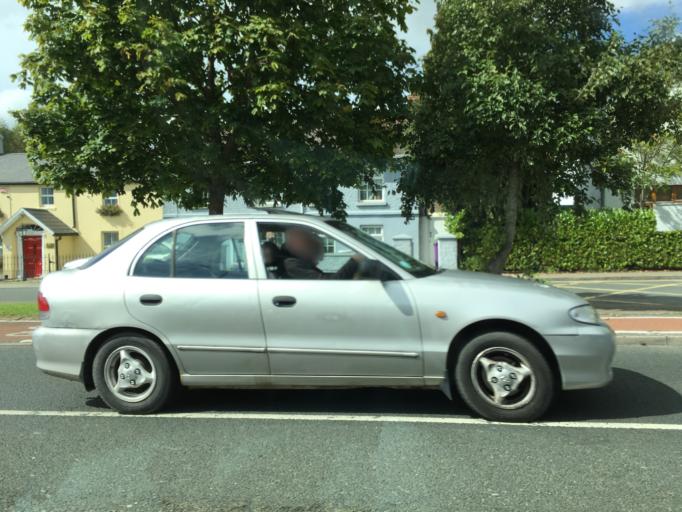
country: IE
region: Leinster
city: Little Bray
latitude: 53.1901
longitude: -6.1252
